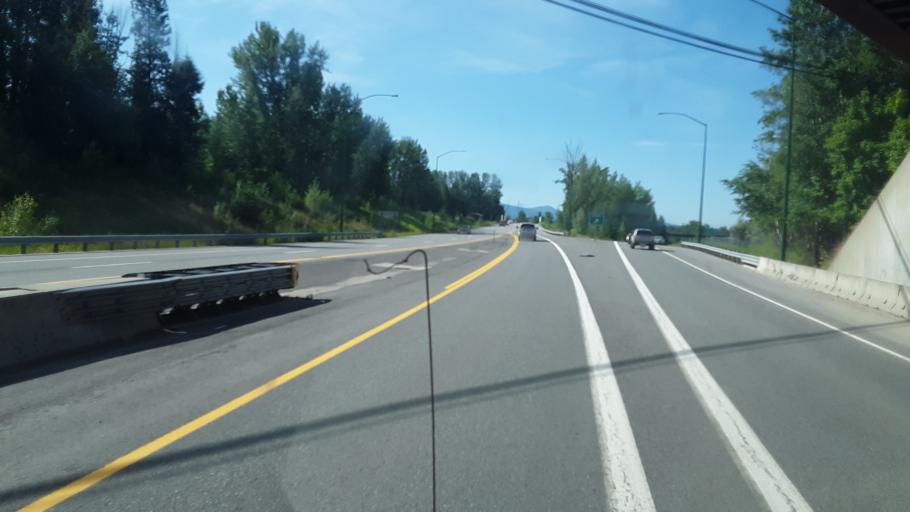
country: US
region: Idaho
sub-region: Bonner County
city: Sandpoint
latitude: 48.2940
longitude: -116.5490
